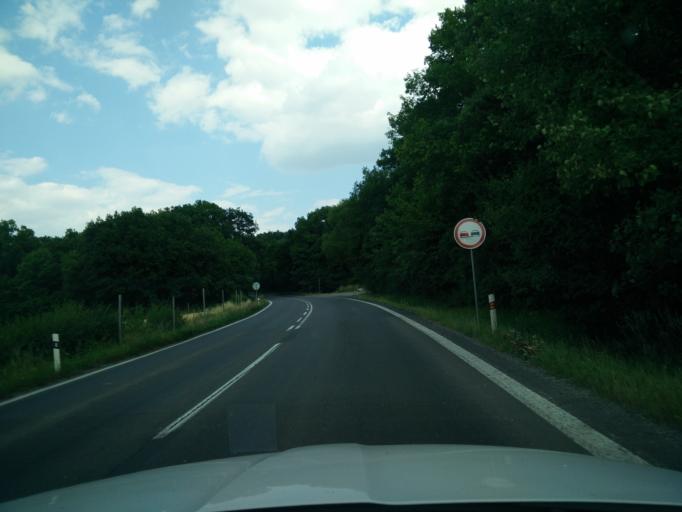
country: SK
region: Nitriansky
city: Novaky
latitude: 48.7205
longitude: 18.5038
